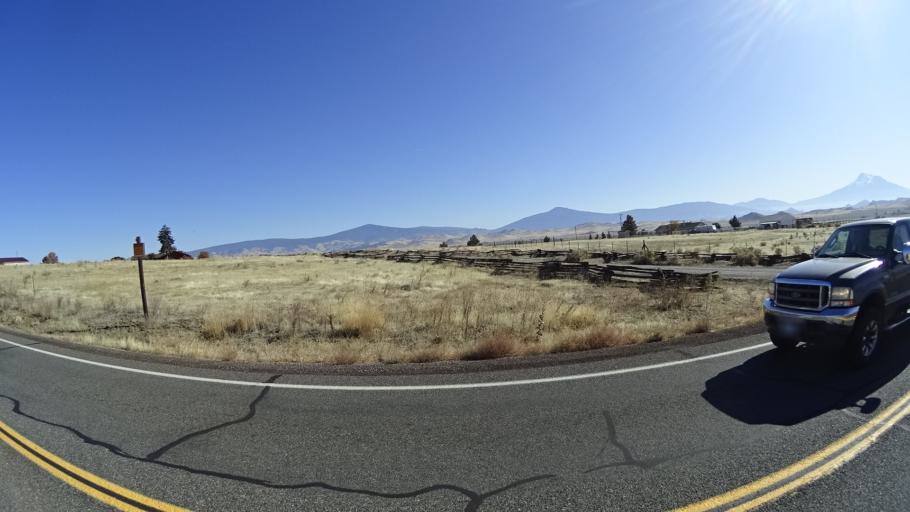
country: US
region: California
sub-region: Siskiyou County
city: Montague
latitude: 41.7728
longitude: -122.5248
